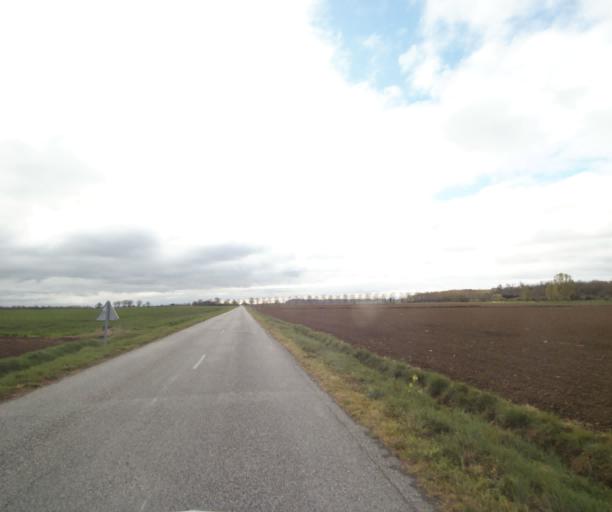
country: FR
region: Midi-Pyrenees
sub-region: Departement de l'Ariege
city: Saverdun
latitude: 43.2550
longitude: 1.5416
